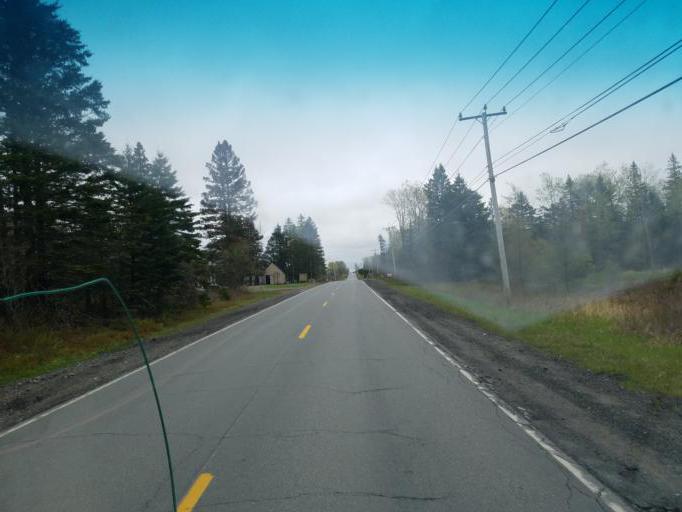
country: US
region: Maine
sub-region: Washington County
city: Eastport
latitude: 44.8305
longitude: -67.0365
